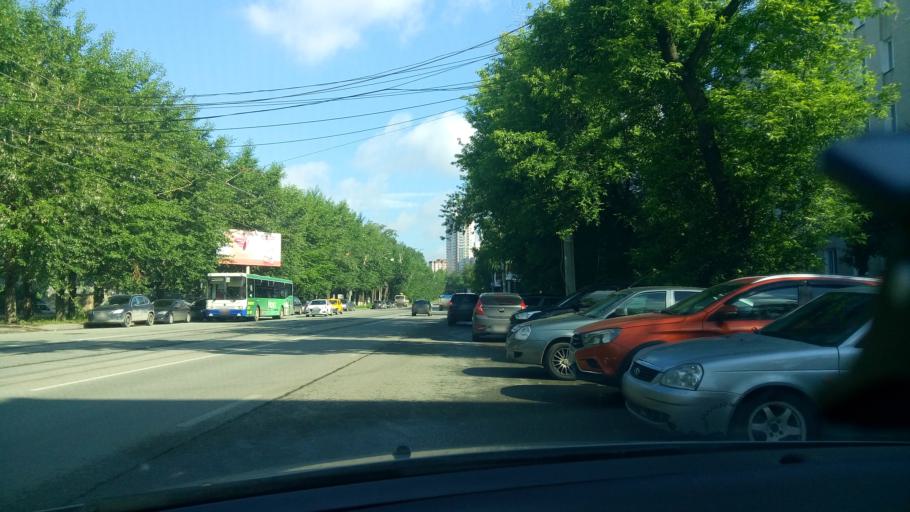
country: RU
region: Sverdlovsk
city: Yekaterinburg
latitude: 56.8463
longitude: 60.6444
